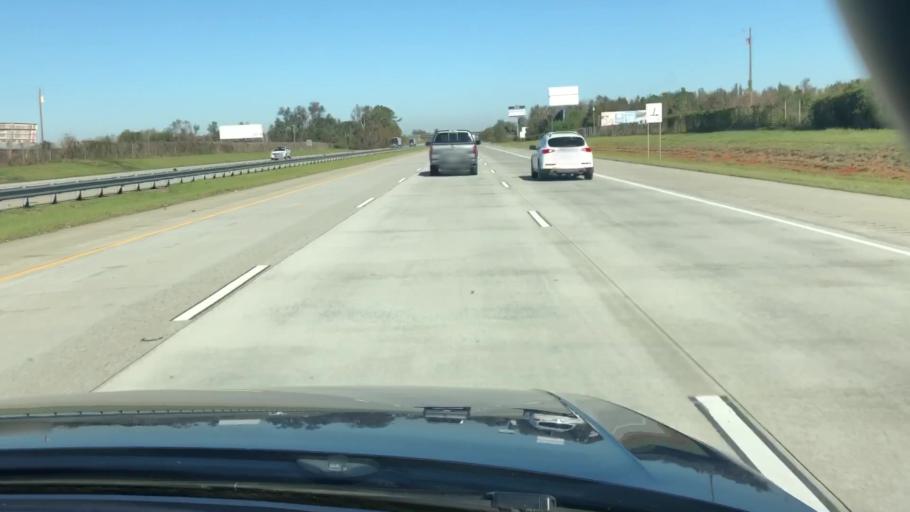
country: US
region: Georgia
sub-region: Dooly County
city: Unadilla
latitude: 32.2822
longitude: -83.7561
